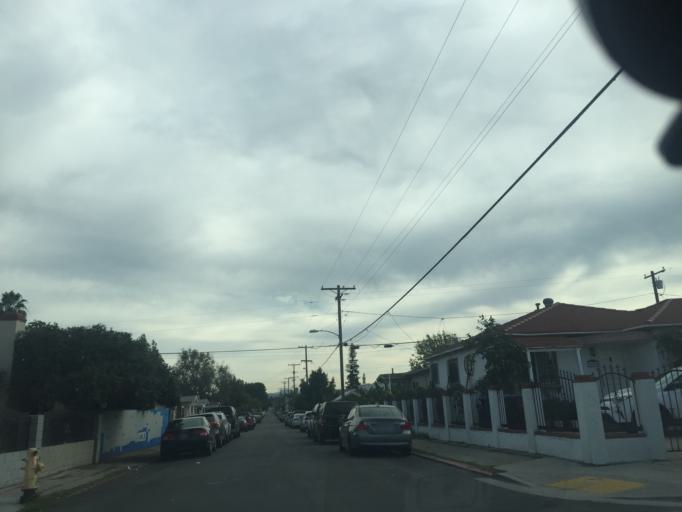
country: US
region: California
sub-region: San Diego County
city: Lemon Grove
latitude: 32.7514
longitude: -117.0977
